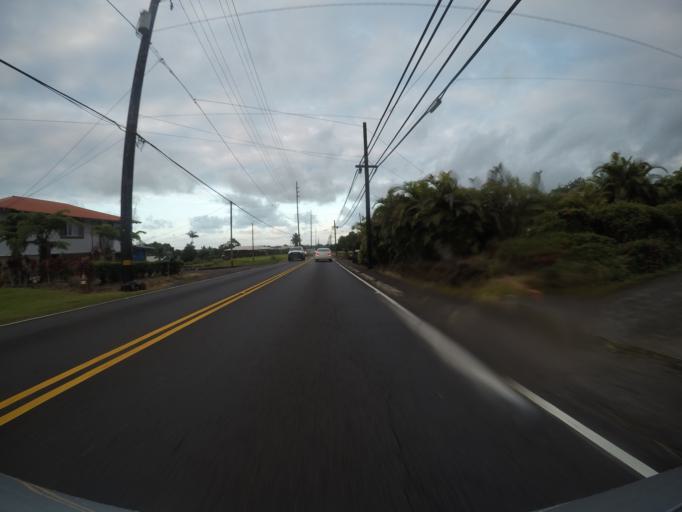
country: US
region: Hawaii
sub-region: Hawaii County
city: Hilo
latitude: 19.6842
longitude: -155.0743
